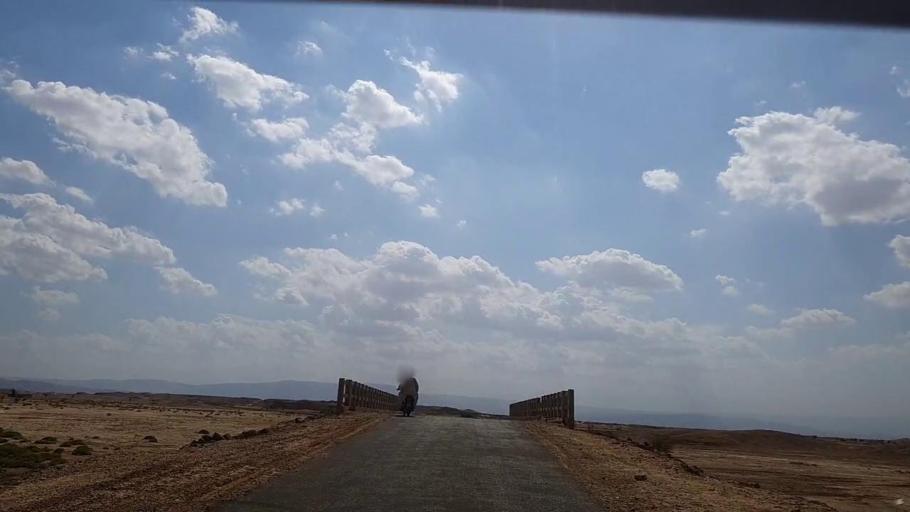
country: PK
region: Sindh
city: Johi
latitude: 26.5278
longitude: 67.5177
